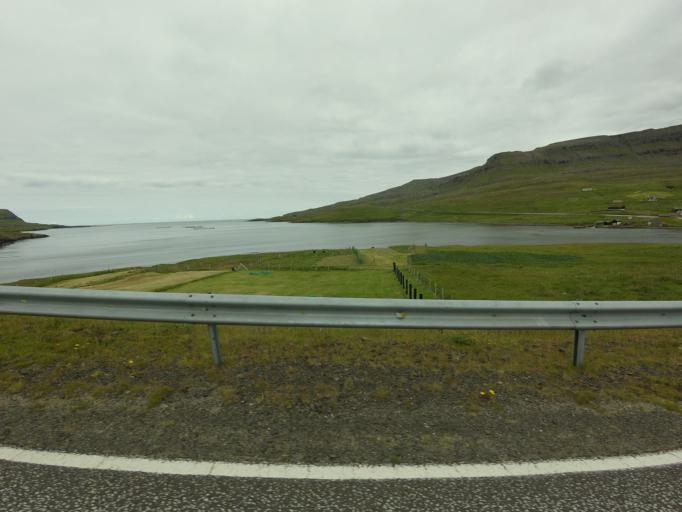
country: FO
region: Suduroy
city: Tvoroyri
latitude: 61.5365
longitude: -6.8111
